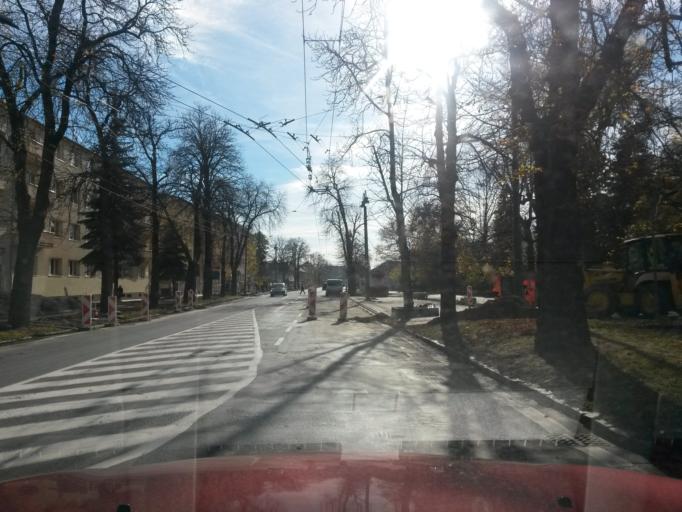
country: SK
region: Presovsky
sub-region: Okres Presov
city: Presov
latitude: 48.9903
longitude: 21.2464
